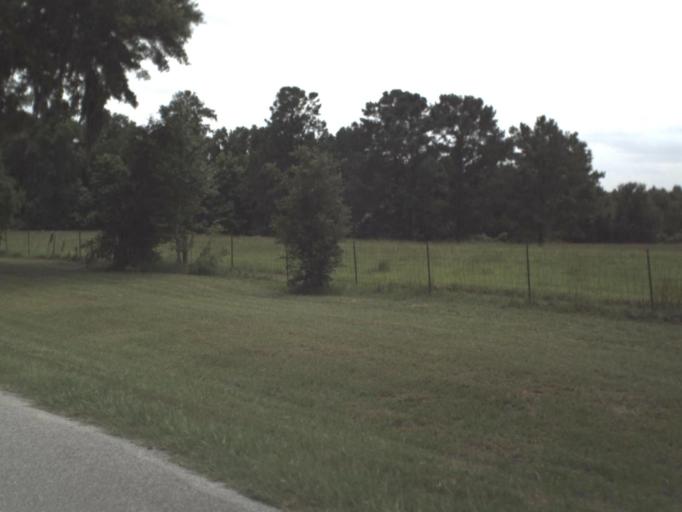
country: US
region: Florida
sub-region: Madison County
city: Madison
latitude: 30.5221
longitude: -83.4226
